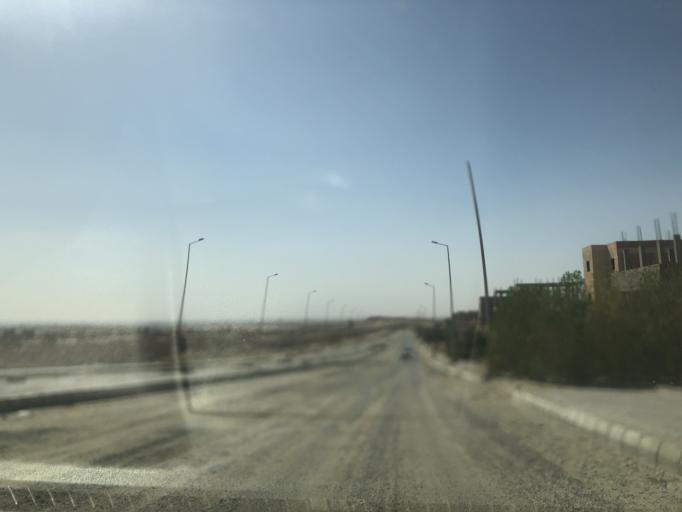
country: EG
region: Al Jizah
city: Madinat Sittah Uktubar
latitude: 29.9302
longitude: 30.9670
